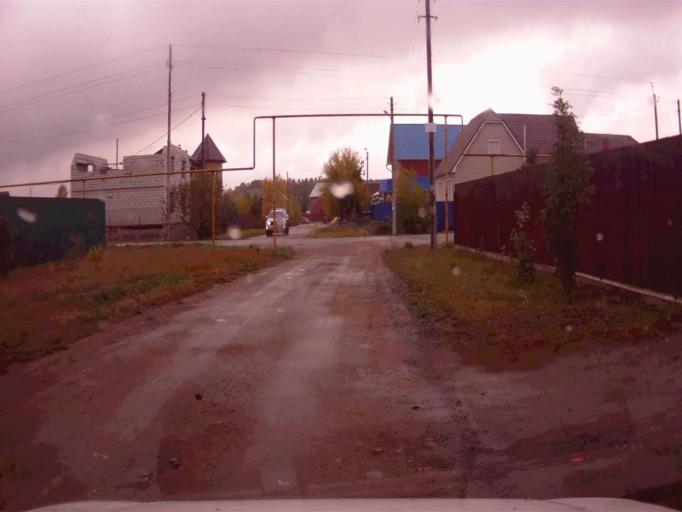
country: RU
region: Chelyabinsk
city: Dolgoderevenskoye
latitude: 55.3054
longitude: 61.3415
